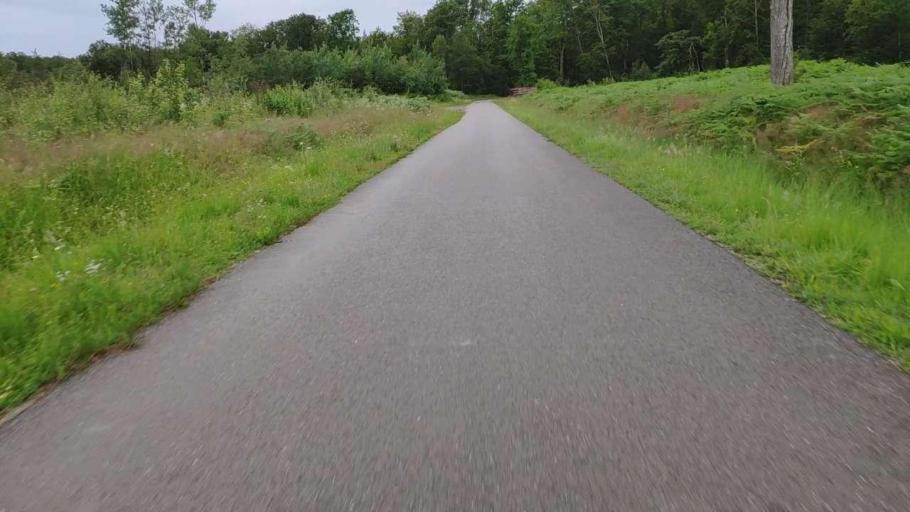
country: FR
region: Franche-Comte
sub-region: Departement du Jura
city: Chaussin
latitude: 46.8953
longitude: 5.4326
